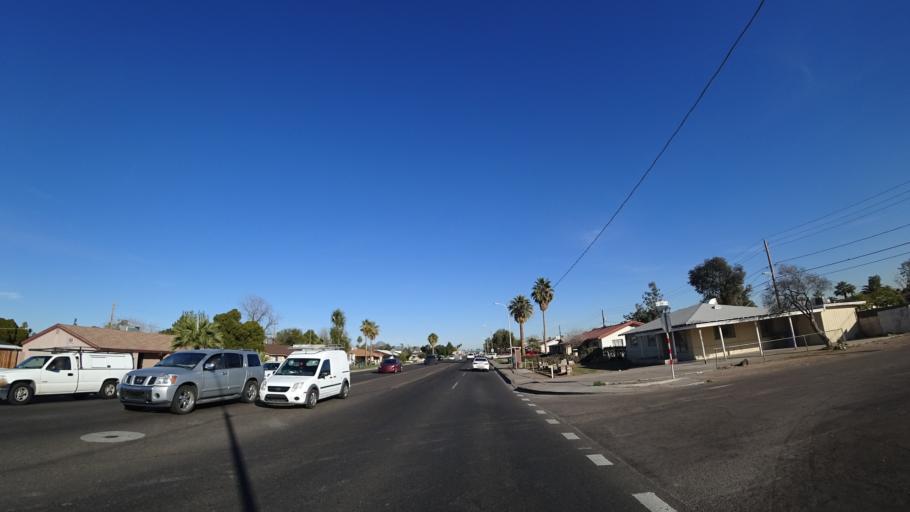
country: US
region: Arizona
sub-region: Maricopa County
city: Glendale
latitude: 33.5239
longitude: -112.1215
